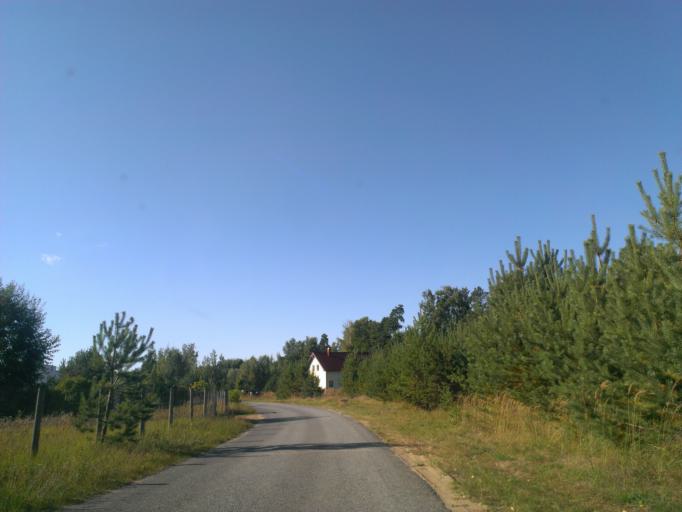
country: LV
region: Adazi
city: Adazi
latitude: 57.0657
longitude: 24.2744
